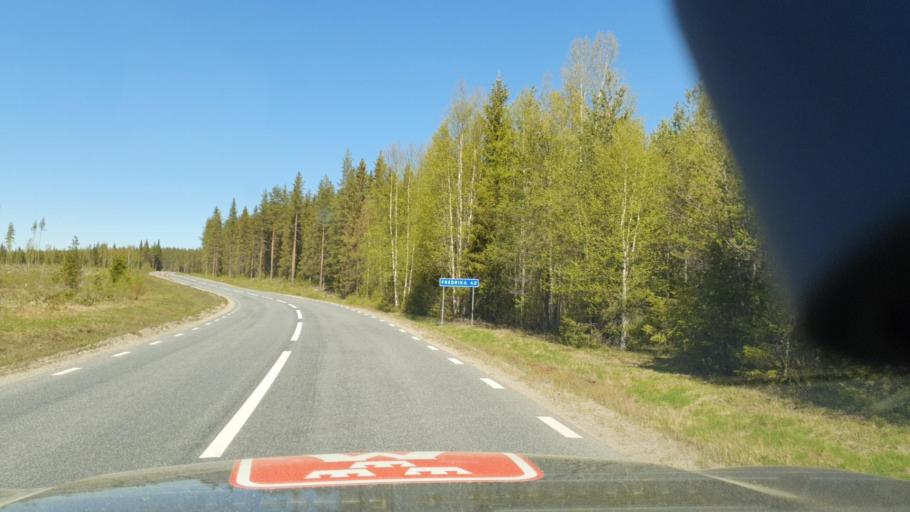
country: SE
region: Vaesternorrland
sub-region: OErnskoeldsviks Kommun
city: Bredbyn
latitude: 63.7481
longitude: 18.4954
